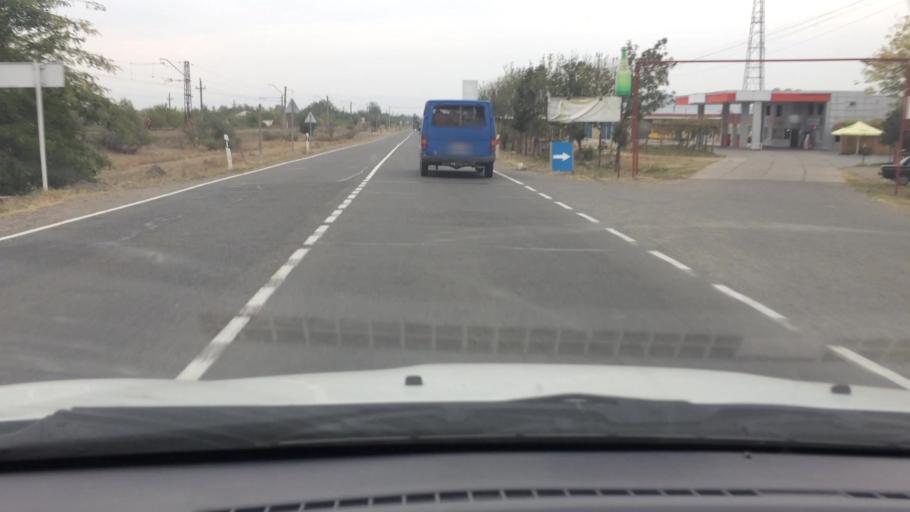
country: GE
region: Kvemo Kartli
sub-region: Marneuli
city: Marneuli
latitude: 41.4388
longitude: 44.8180
